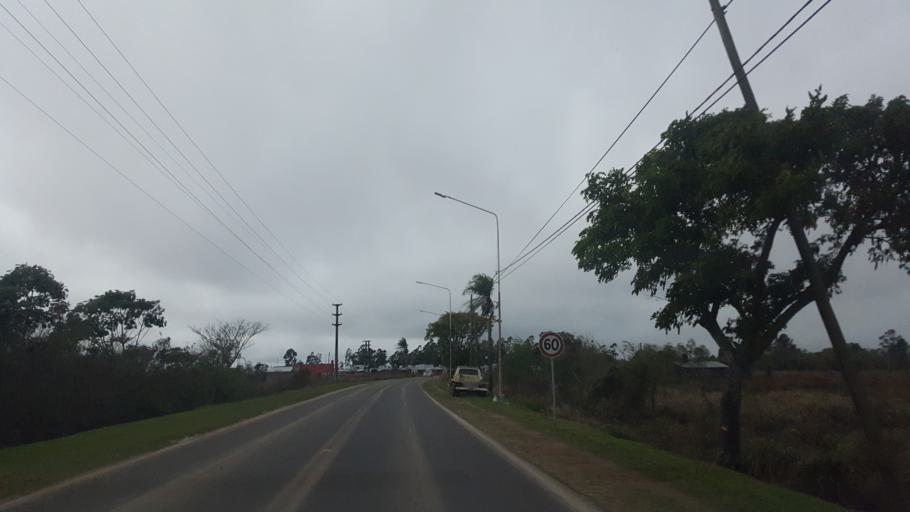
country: AR
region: Corrientes
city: Ituzaingo
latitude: -27.5940
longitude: -56.6814
